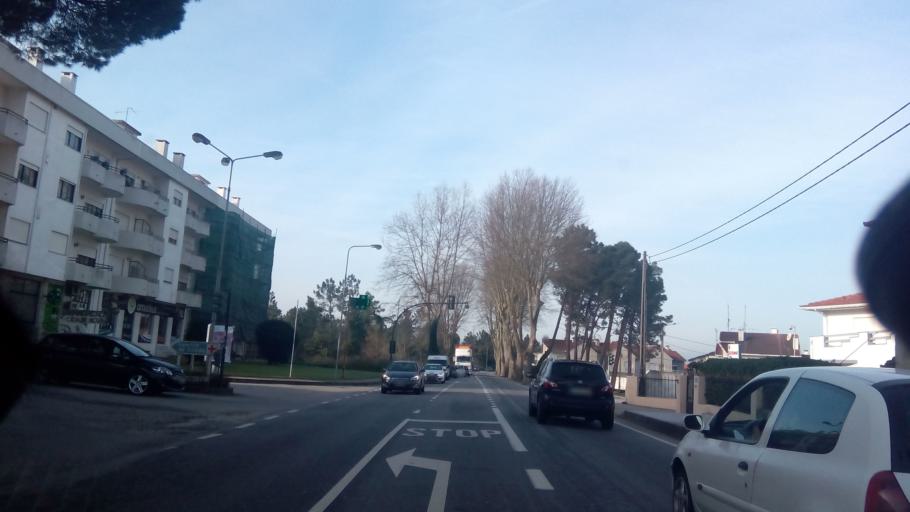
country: PT
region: Viana do Castelo
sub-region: Viana do Castelo
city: Meadela
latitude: 41.6810
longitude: -8.8024
